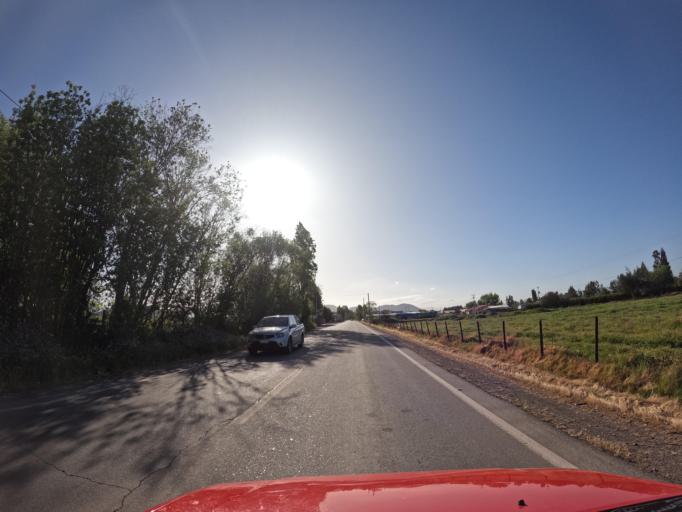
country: CL
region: O'Higgins
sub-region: Provincia de Colchagua
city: Santa Cruz
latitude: -34.7371
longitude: -71.2606
